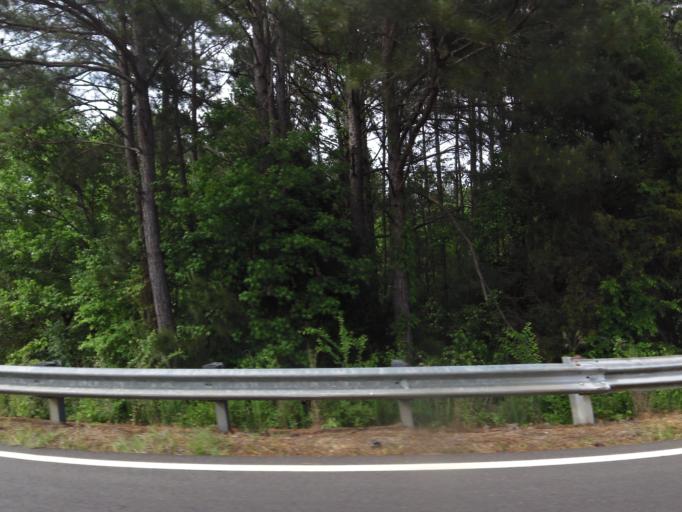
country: US
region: Georgia
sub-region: McDuffie County
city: Thomson
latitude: 33.5236
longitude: -82.4646
